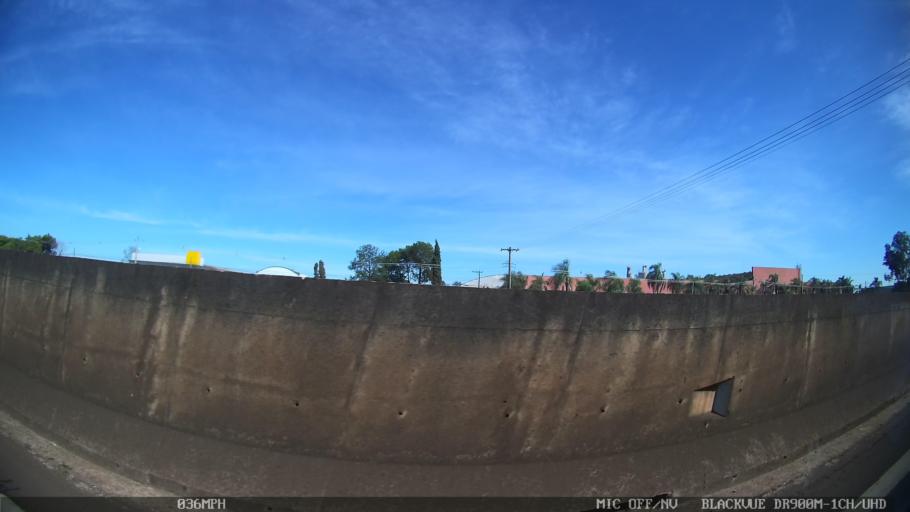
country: BR
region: Sao Paulo
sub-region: Leme
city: Leme
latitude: -22.1994
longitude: -47.3960
